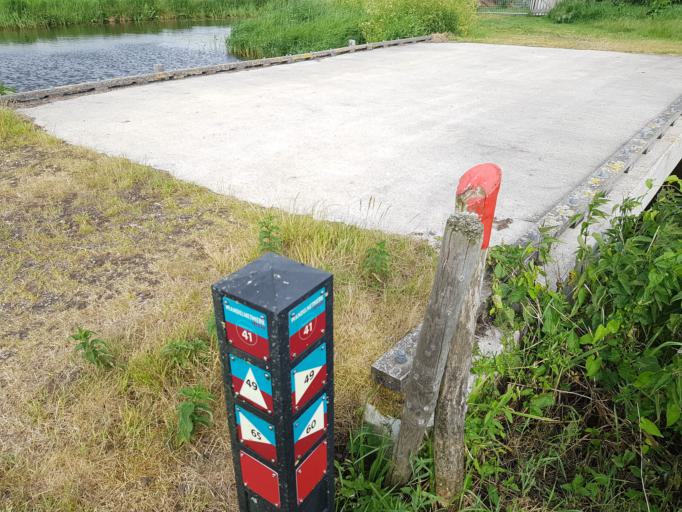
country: NL
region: Friesland
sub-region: Gemeente Smallingerland
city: Oudega
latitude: 53.0890
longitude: 5.9689
